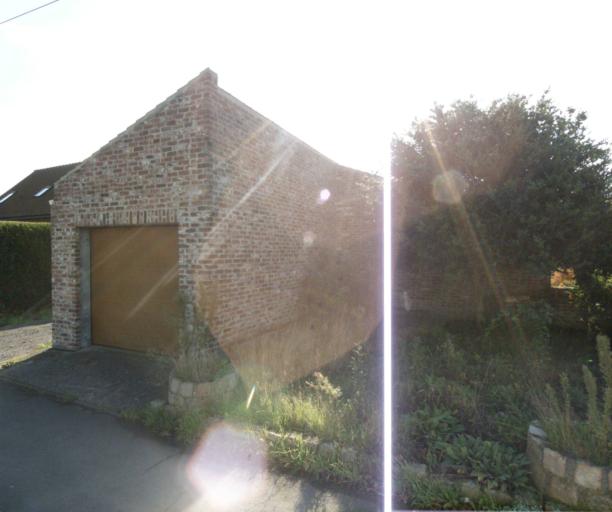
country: FR
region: Nord-Pas-de-Calais
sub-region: Departement du Nord
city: Lompret
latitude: 50.6733
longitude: 2.9837
